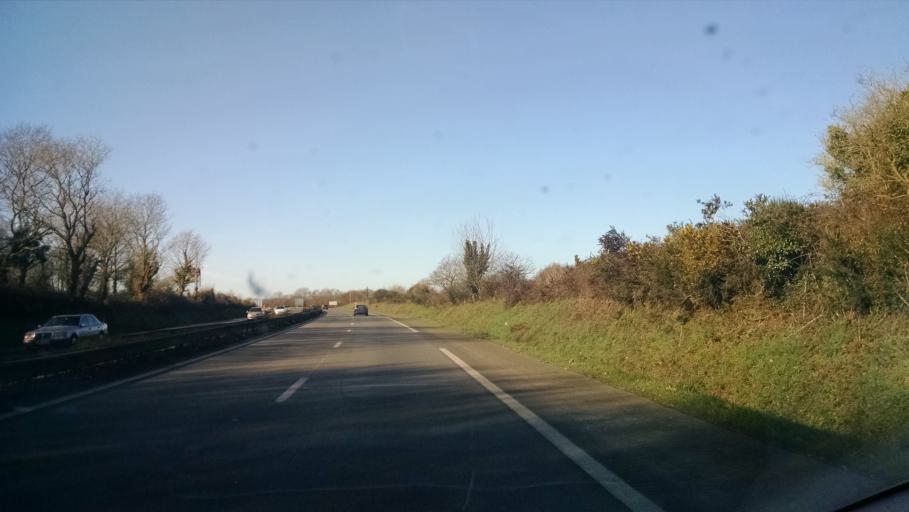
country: FR
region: Brittany
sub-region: Departement du Morbihan
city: Queven
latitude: 47.7780
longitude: -3.4002
